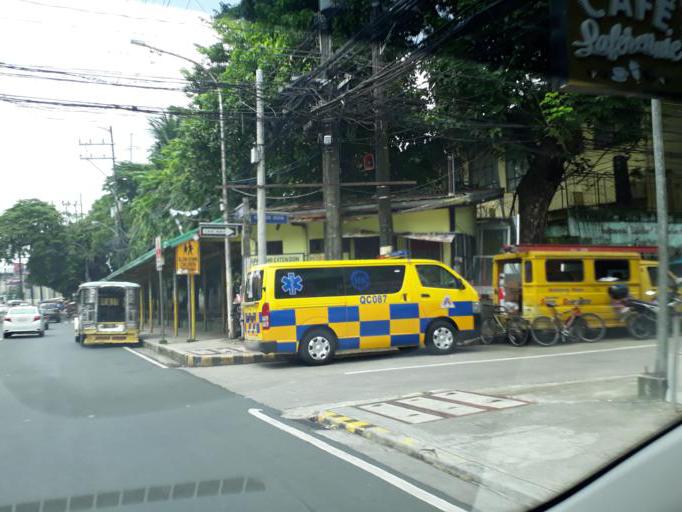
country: PH
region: Metro Manila
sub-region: Quezon City
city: Quezon City
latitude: 14.6304
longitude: 121.0388
